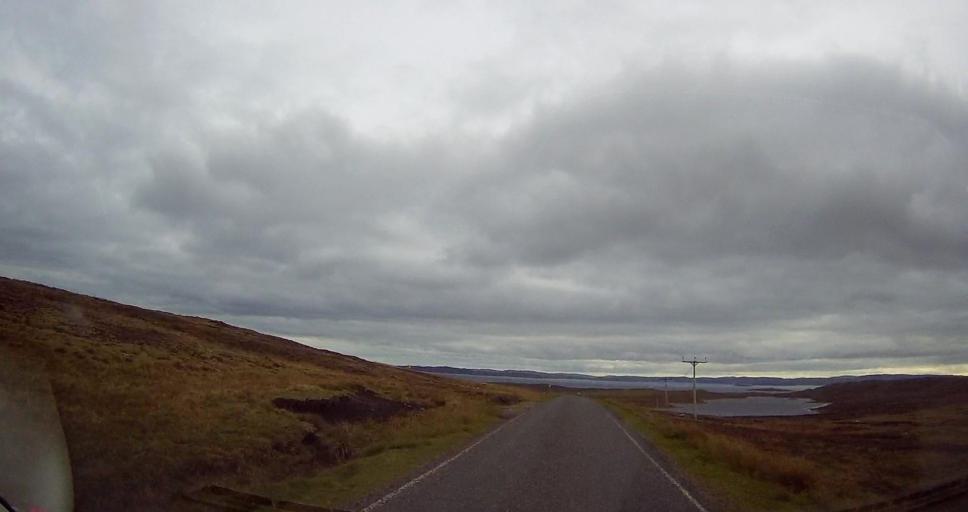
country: GB
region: Scotland
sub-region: Shetland Islands
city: Shetland
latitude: 60.5154
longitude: -1.0584
